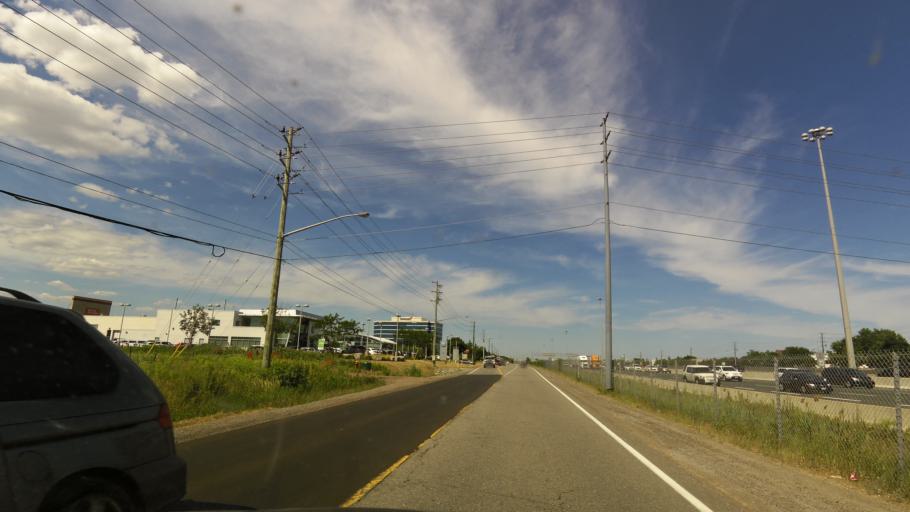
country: CA
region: Ontario
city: Oakville
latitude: 43.4285
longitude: -79.7208
